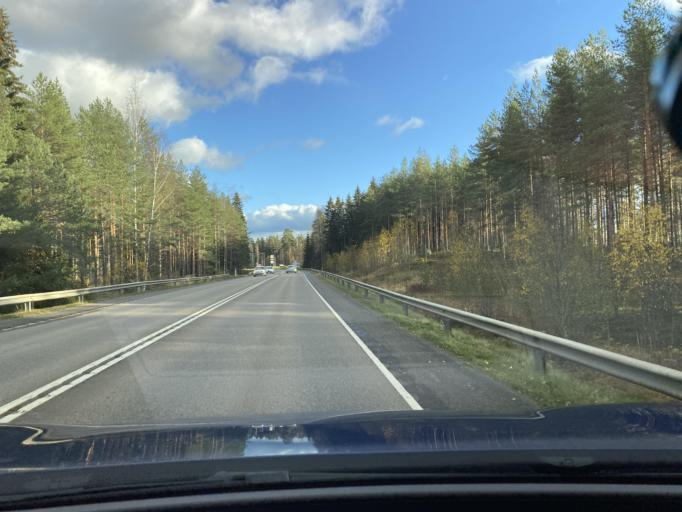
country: FI
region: Haeme
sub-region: Riihimaeki
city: Oitti
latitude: 60.7926
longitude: 24.9904
